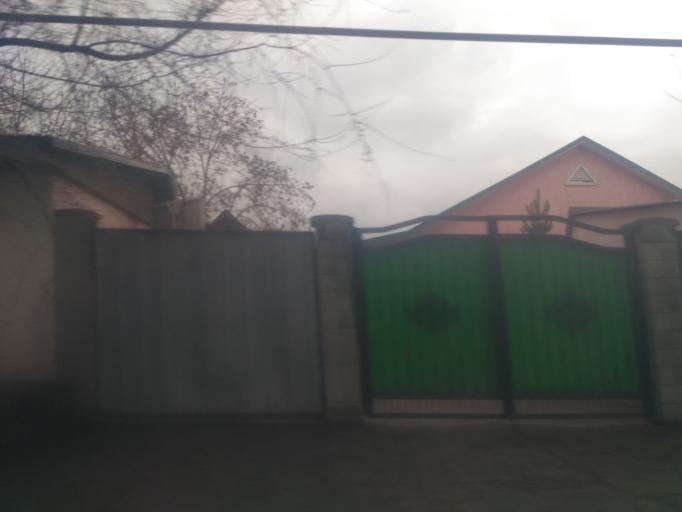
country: KZ
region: Almaty Oblysy
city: Burunday
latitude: 43.2181
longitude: 76.7576
